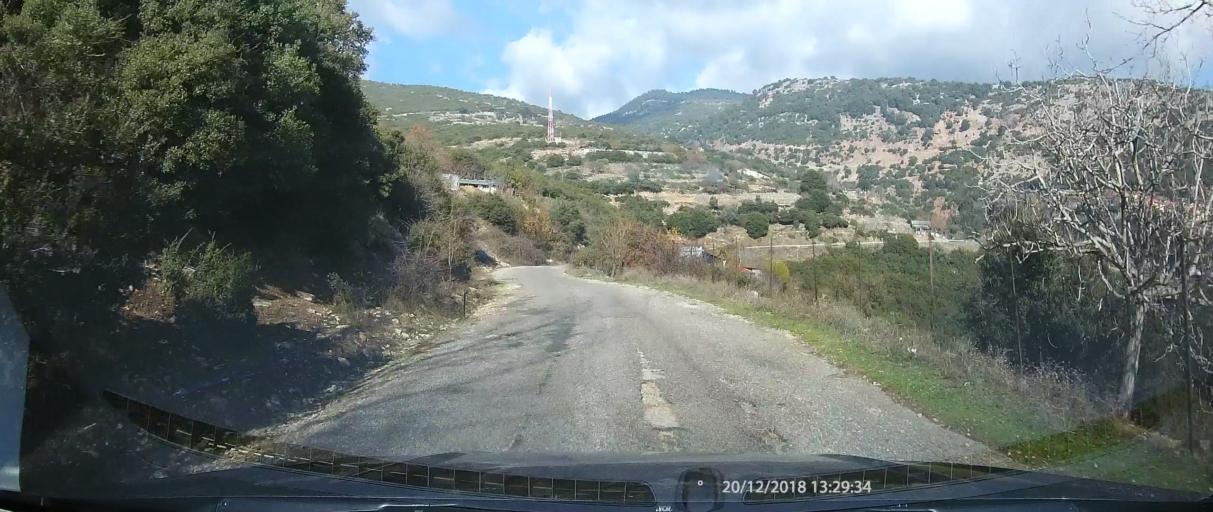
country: GR
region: West Greece
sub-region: Nomos Aitolias kai Akarnanias
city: Paravola
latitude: 38.6299
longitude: 21.5800
